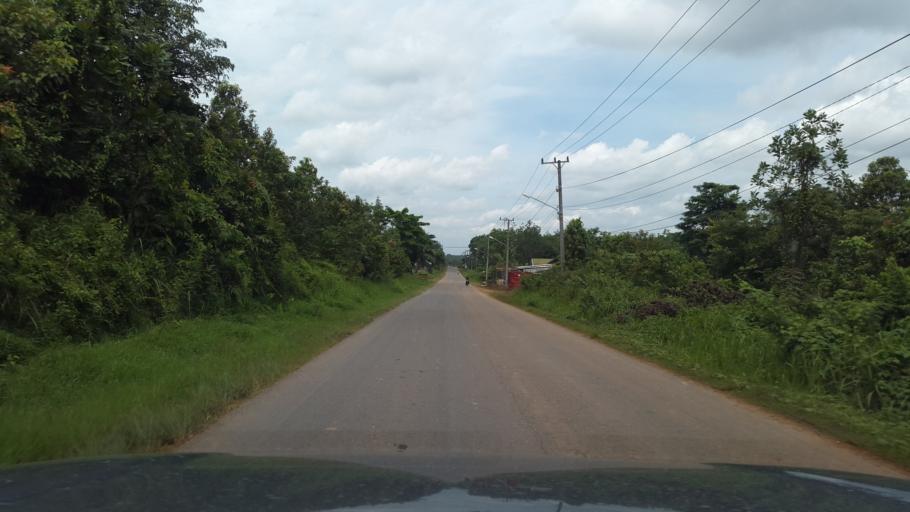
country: ID
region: South Sumatra
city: Gunungmegang Dalam
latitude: -3.3275
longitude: 103.9052
